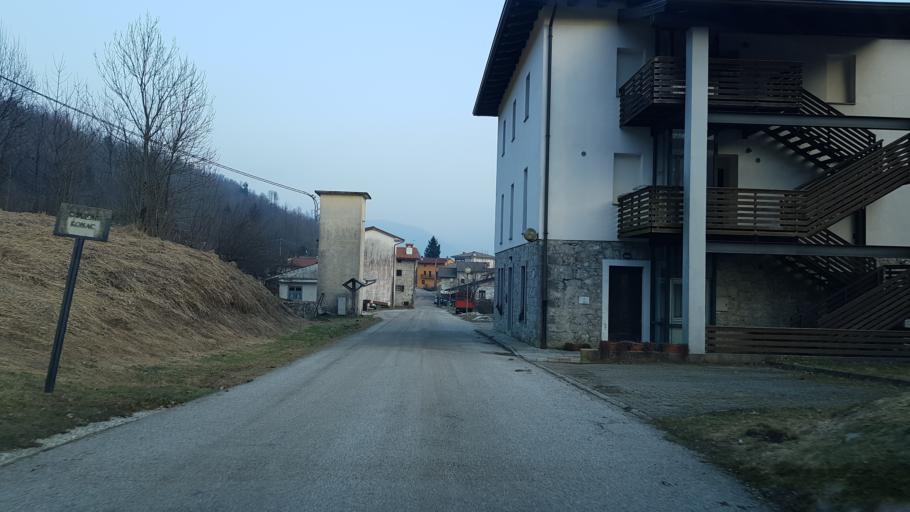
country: IT
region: Friuli Venezia Giulia
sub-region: Provincia di Udine
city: Taipana
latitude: 46.2417
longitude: 13.3833
